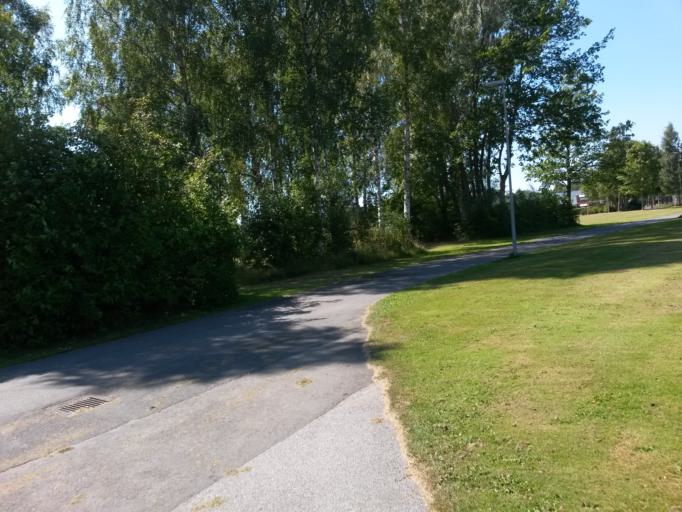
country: SE
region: Vaestra Goetaland
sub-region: Lidkopings Kommun
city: Lidkoping
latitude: 58.4868
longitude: 13.1485
